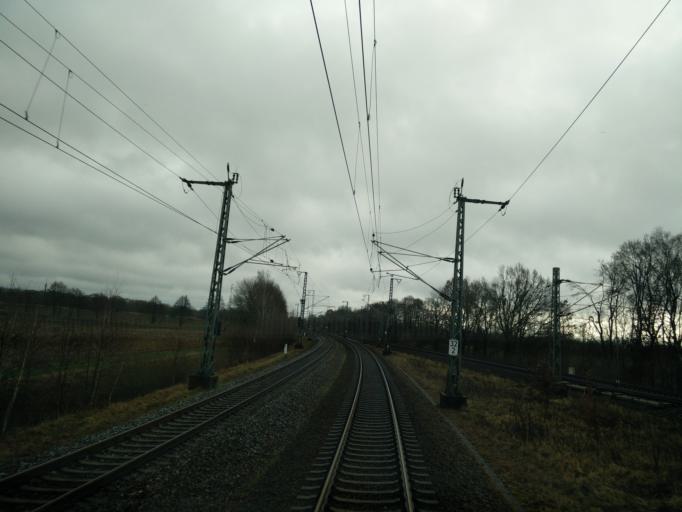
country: DE
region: Mecklenburg-Vorpommern
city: Ludwigslust
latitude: 53.3460
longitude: 11.4714
